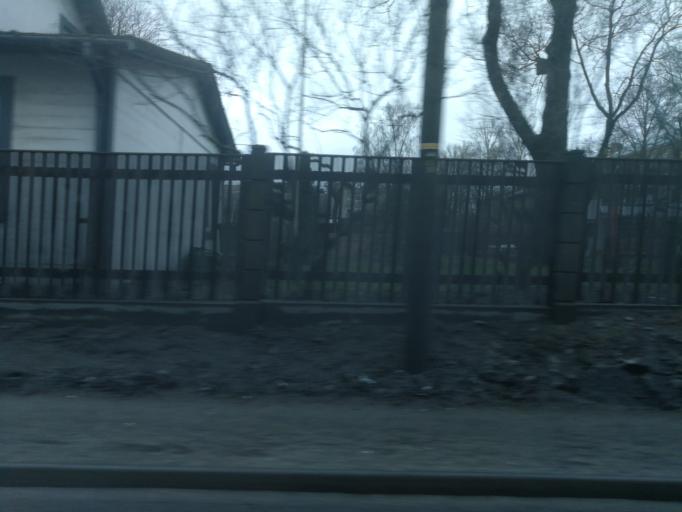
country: LV
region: Riga
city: Bolderaja
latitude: 57.0316
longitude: 24.1149
